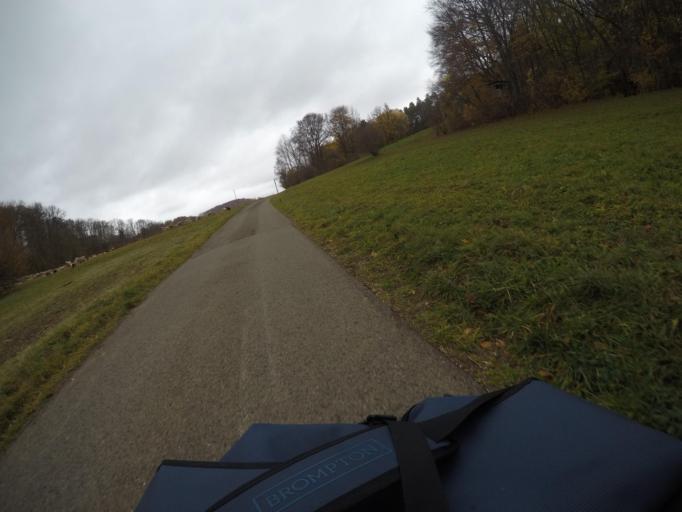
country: DE
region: Baden-Wuerttemberg
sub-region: Tuebingen Region
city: Pfullingen
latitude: 48.4041
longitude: 9.2441
